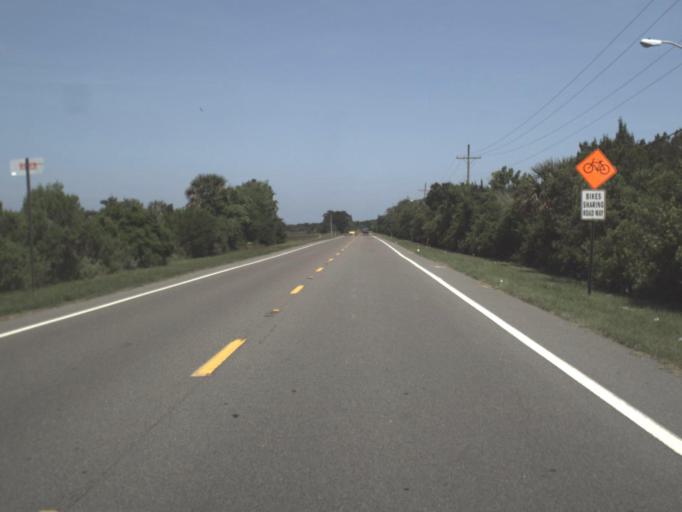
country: US
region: Florida
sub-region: Duval County
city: Atlantic Beach
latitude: 30.3991
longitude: -81.4731
